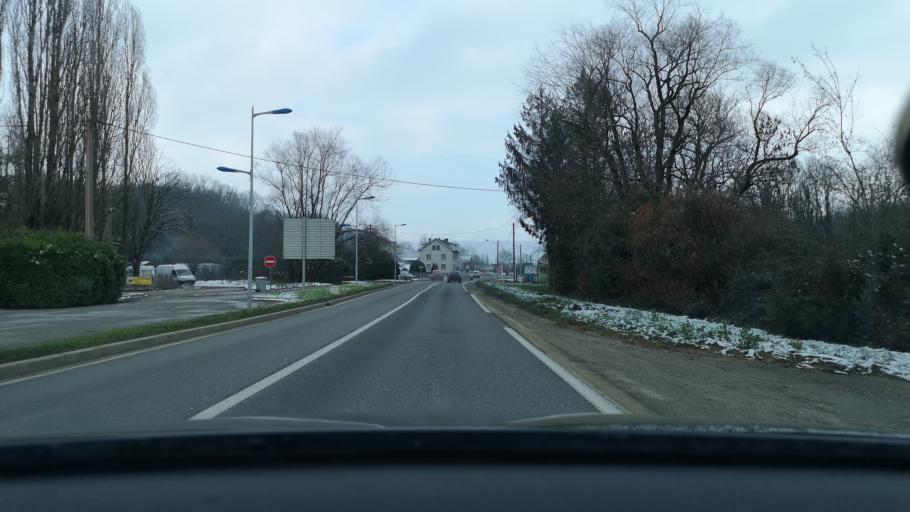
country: FR
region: Franche-Comte
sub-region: Departement du Jura
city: Montmorot
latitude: 46.6776
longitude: 5.5126
